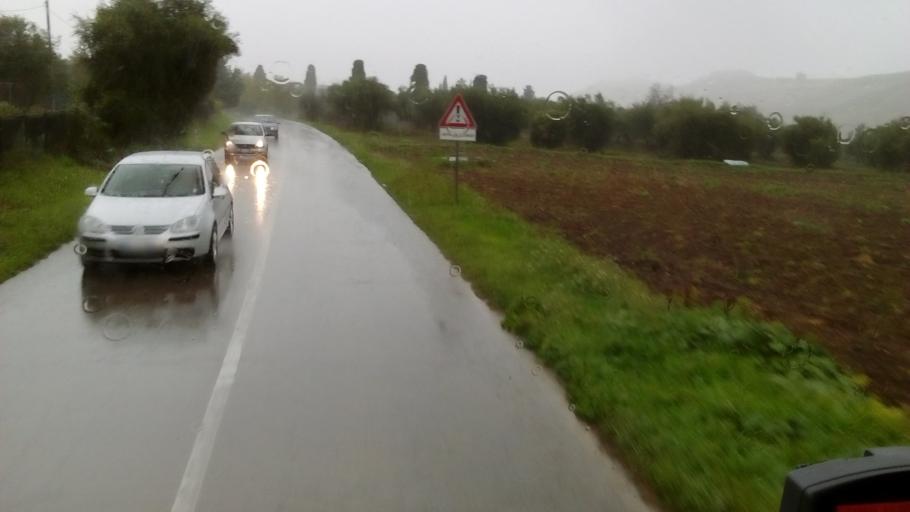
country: IT
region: Sicily
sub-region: Enna
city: Pietraperzia
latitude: 37.4211
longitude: 14.1639
